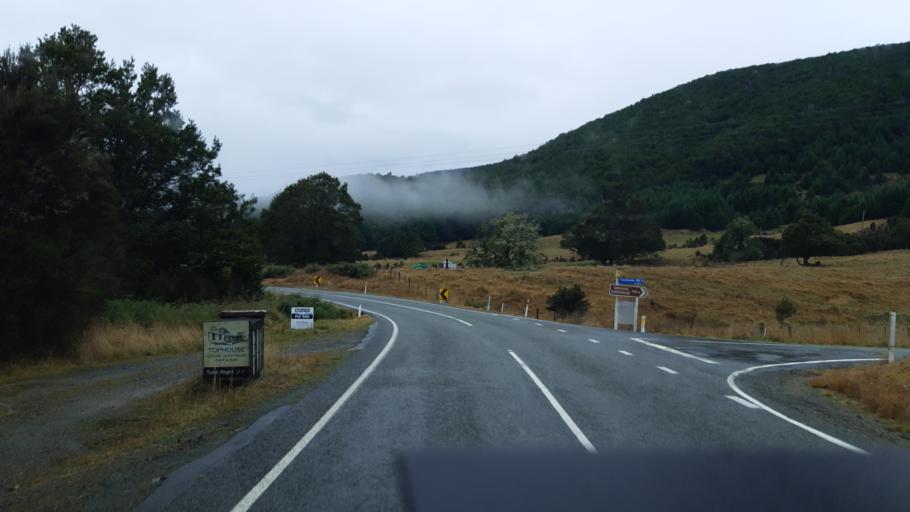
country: NZ
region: Tasman
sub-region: Tasman District
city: Wakefield
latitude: -41.7589
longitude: 172.8996
